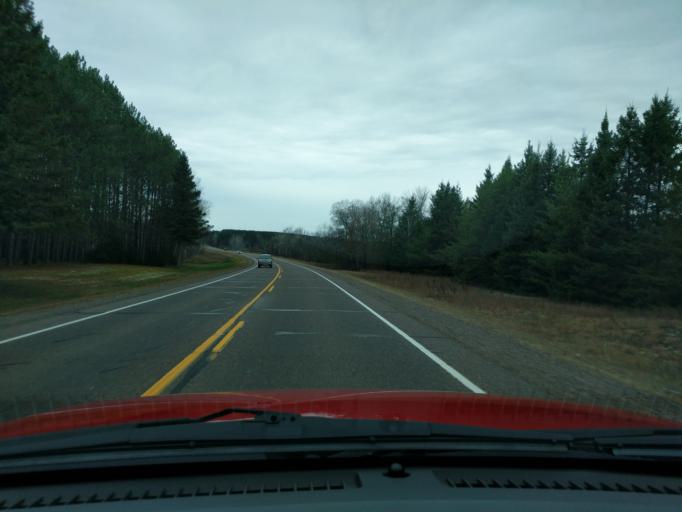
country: US
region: Wisconsin
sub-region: Washburn County
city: Spooner
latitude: 45.8239
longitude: -91.9449
